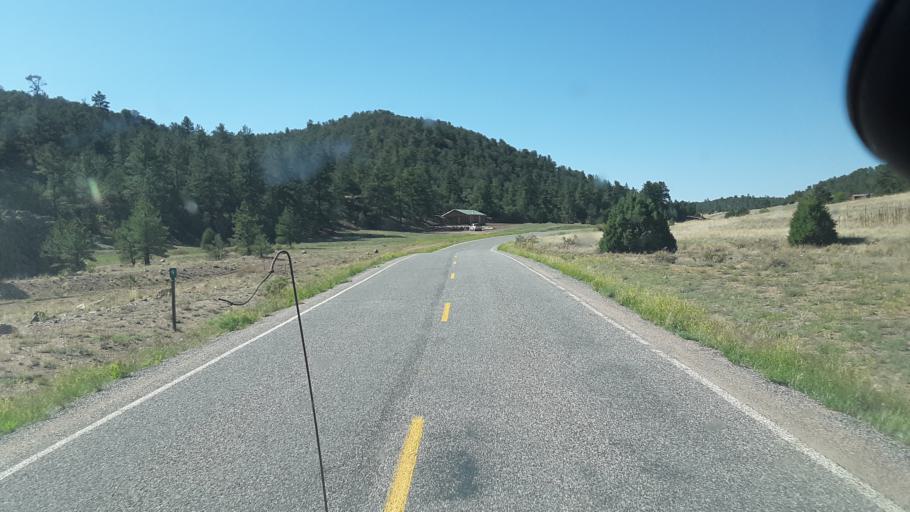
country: US
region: Colorado
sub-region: Fremont County
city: Canon City
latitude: 38.3827
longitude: -105.4562
